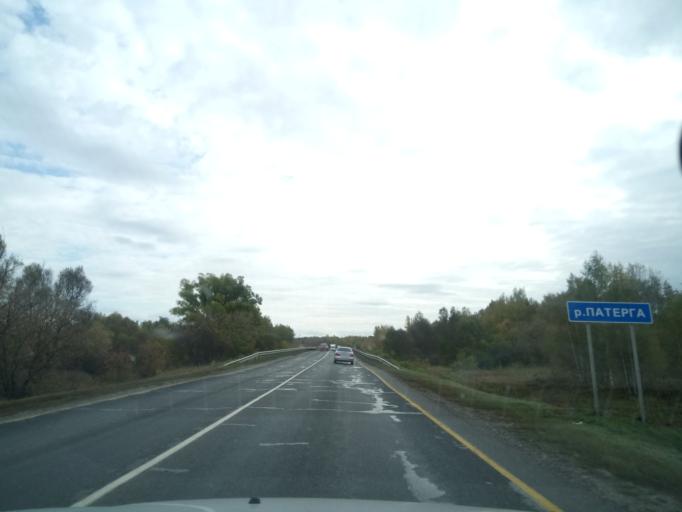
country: RU
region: Nizjnij Novgorod
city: Lukoyanov
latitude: 55.0560
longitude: 44.3686
